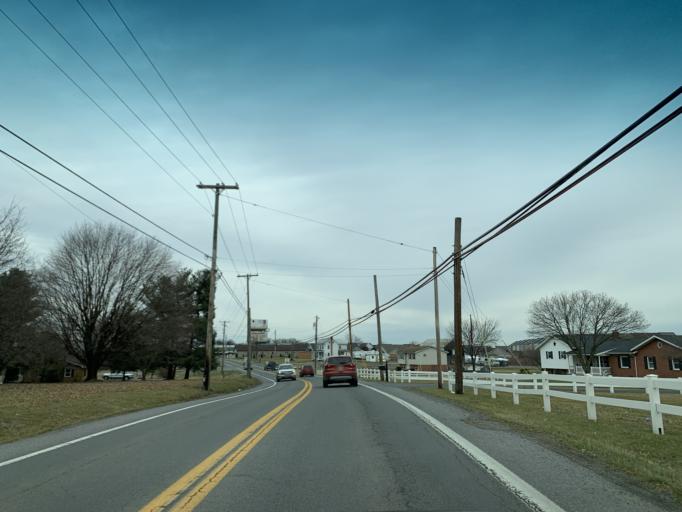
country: US
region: West Virginia
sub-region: Berkeley County
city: Martinsburg
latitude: 39.5336
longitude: -77.9121
